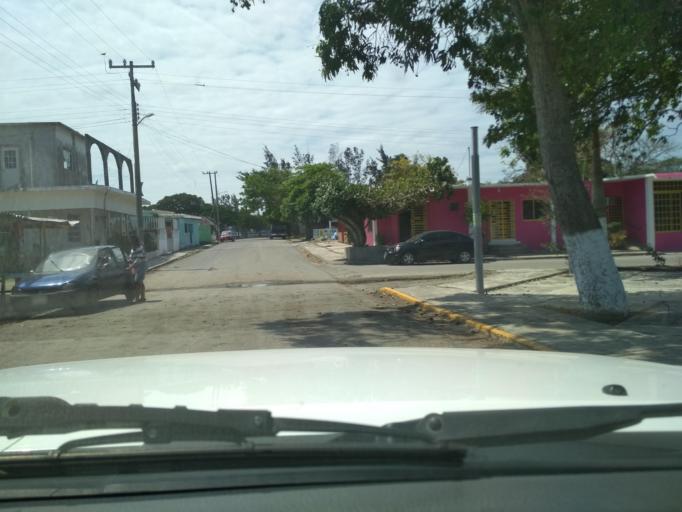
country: MX
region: Veracruz
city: Anton Lizardo
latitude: 19.0044
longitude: -95.9894
